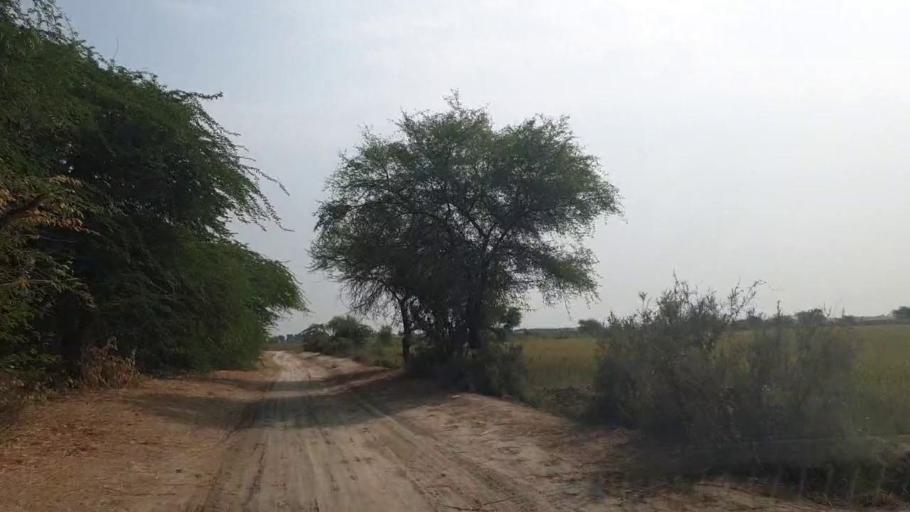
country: PK
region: Sindh
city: Badin
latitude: 24.7634
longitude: 68.7825
